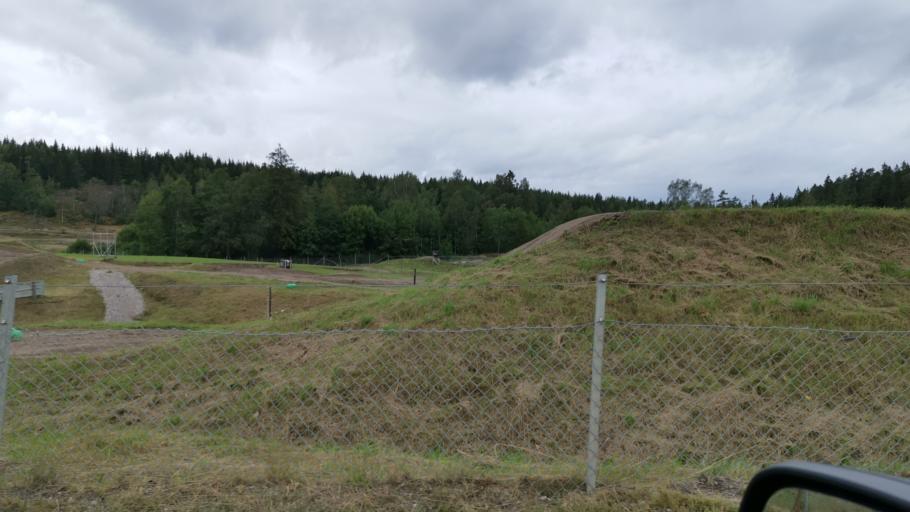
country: SE
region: Vaestra Goetaland
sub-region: Uddevalla Kommun
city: Uddevalla
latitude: 58.3400
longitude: 12.0209
